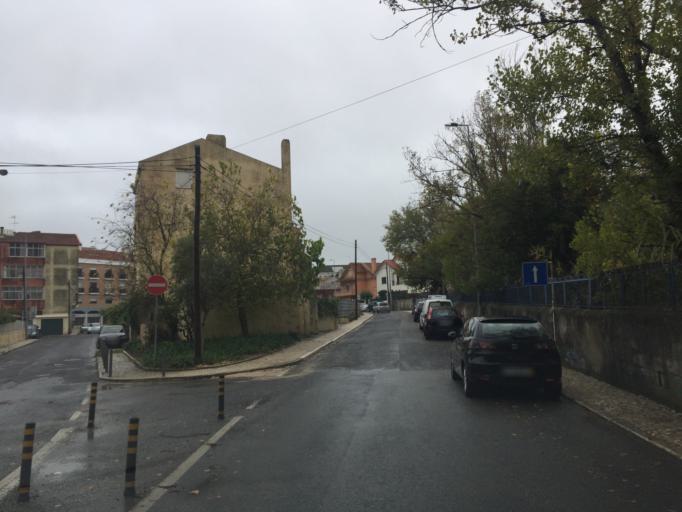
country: PT
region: Lisbon
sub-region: Sintra
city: Rio de Mouro
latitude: 38.7925
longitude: -9.3465
